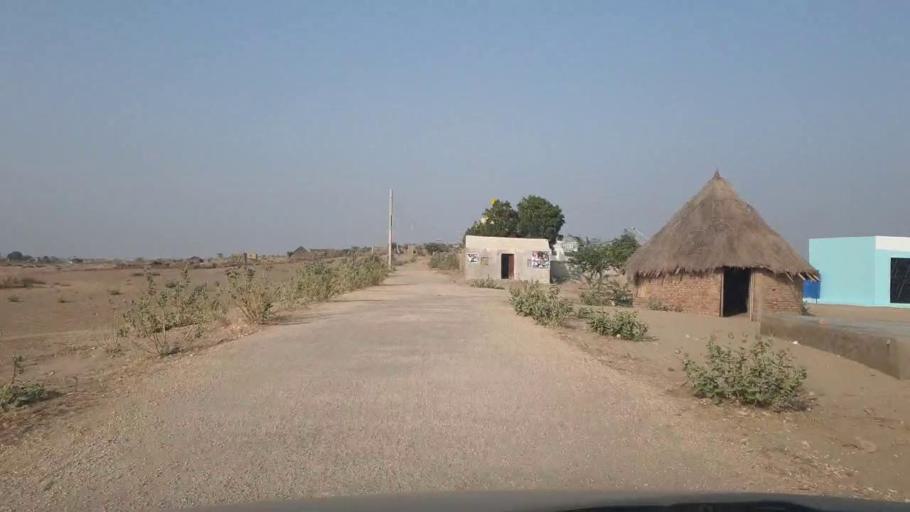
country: PK
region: Sindh
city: Umarkot
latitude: 25.3439
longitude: 69.7649
